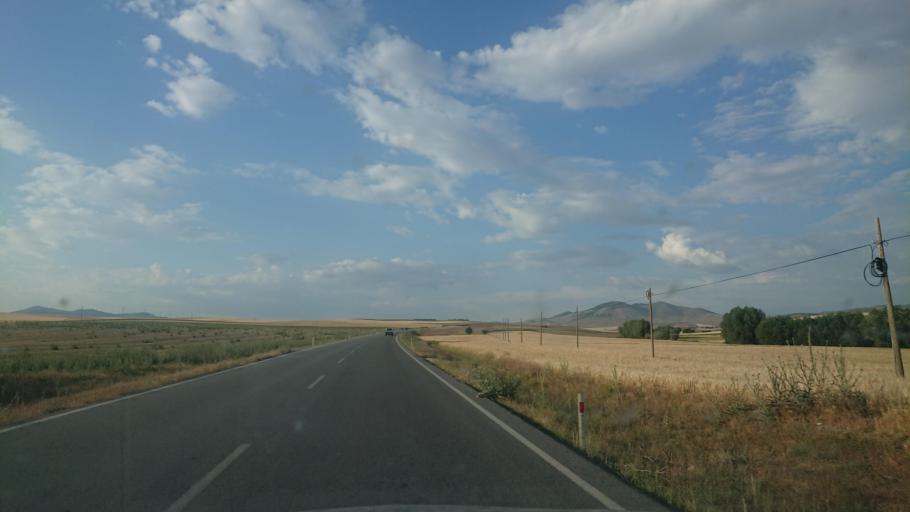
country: TR
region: Aksaray
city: Aksaray
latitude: 38.4851
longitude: 34.0674
